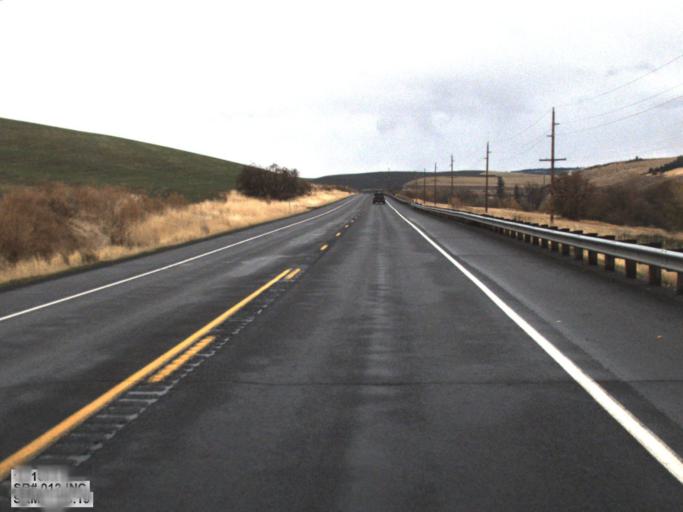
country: US
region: Washington
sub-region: Walla Walla County
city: Walla Walla East
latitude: 46.1298
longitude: -118.1859
